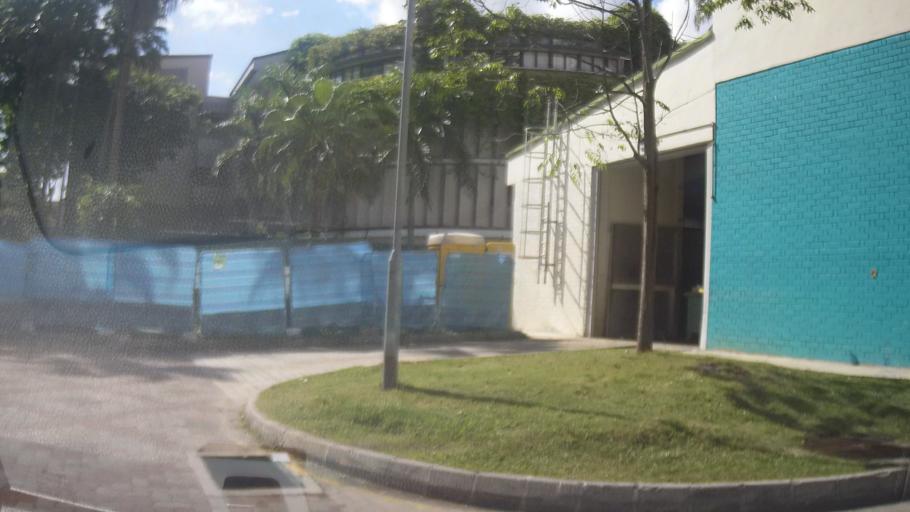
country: MY
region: Johor
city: Johor Bahru
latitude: 1.4269
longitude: 103.7751
